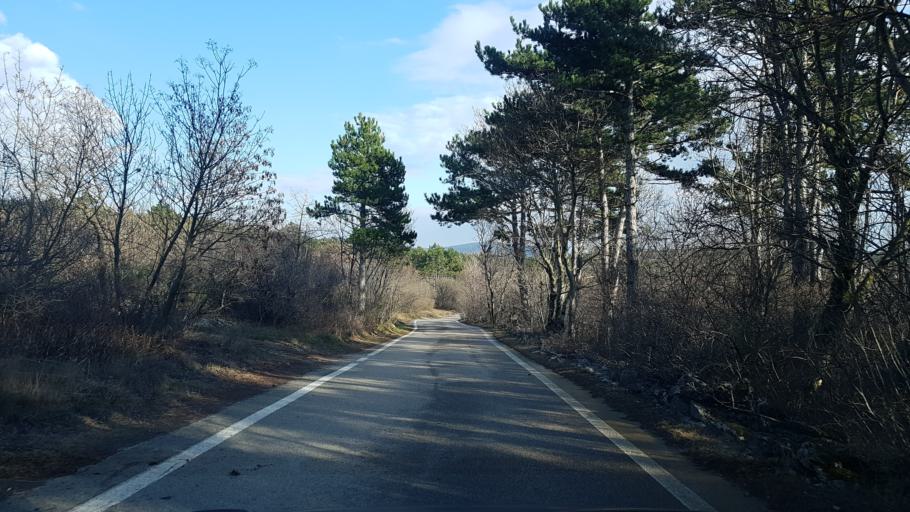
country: IT
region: Friuli Venezia Giulia
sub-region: Provincia di Trieste
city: Dolina
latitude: 45.6290
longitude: 13.8684
